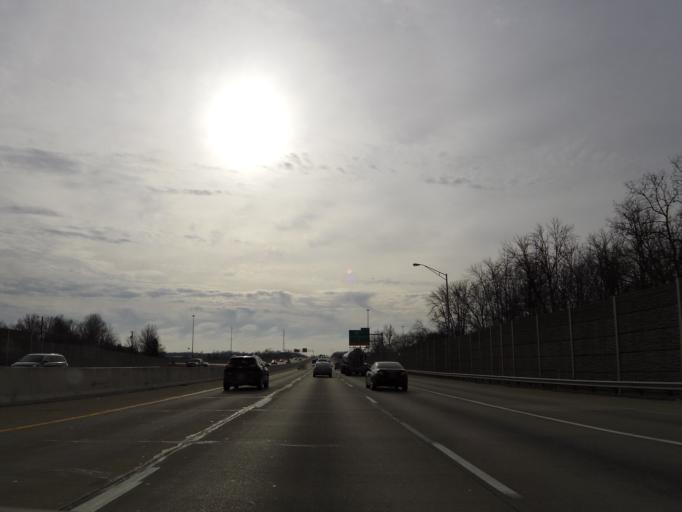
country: US
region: Indiana
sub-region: Marion County
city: Warren Park
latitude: 39.7781
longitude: -86.0313
